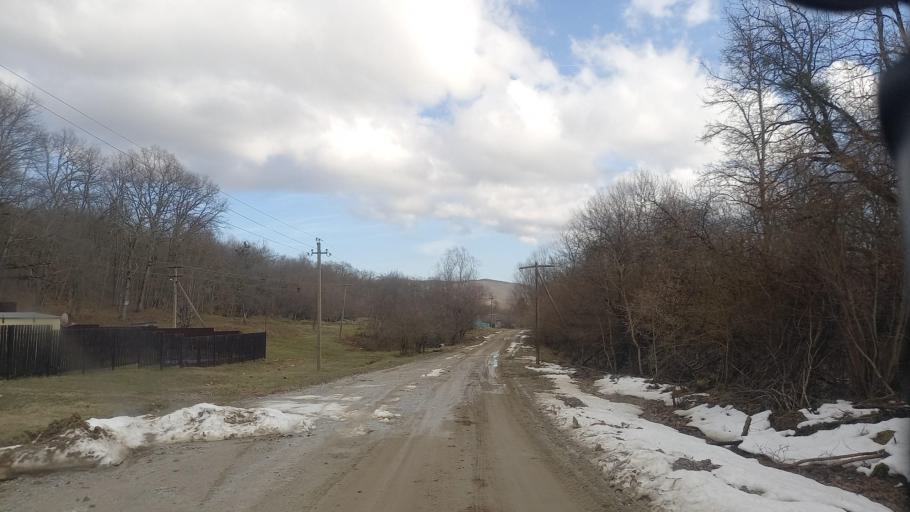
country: RU
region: Krasnodarskiy
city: Smolenskaya
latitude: 44.6028
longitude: 38.8641
